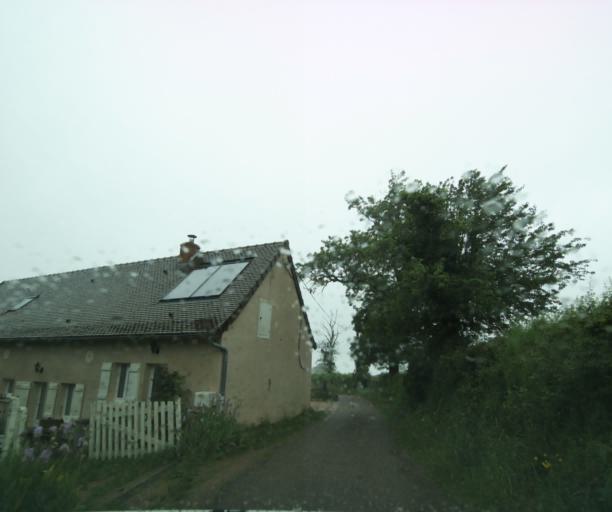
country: FR
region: Bourgogne
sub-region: Departement de Saone-et-Loire
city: La Clayette
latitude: 46.3675
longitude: 4.3527
